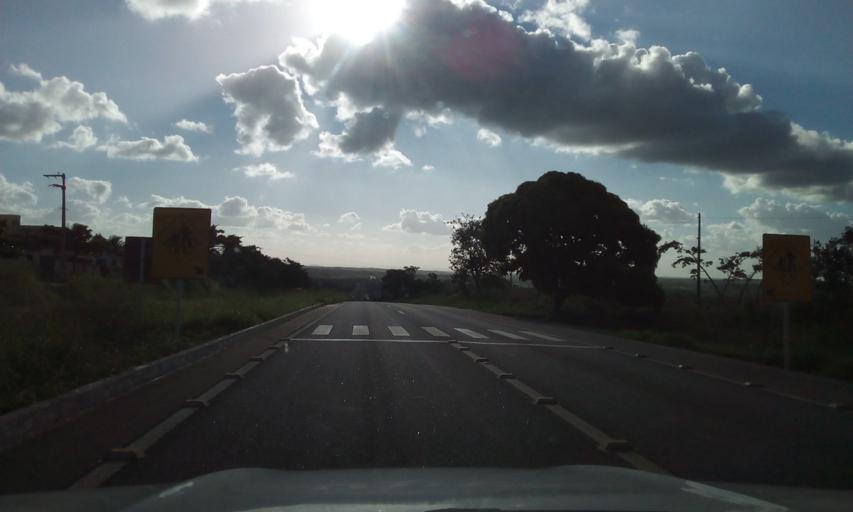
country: BR
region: Paraiba
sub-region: Cruz Do Espirito Santo
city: Cruz do Espirito Santo
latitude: -7.2025
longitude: -35.1563
